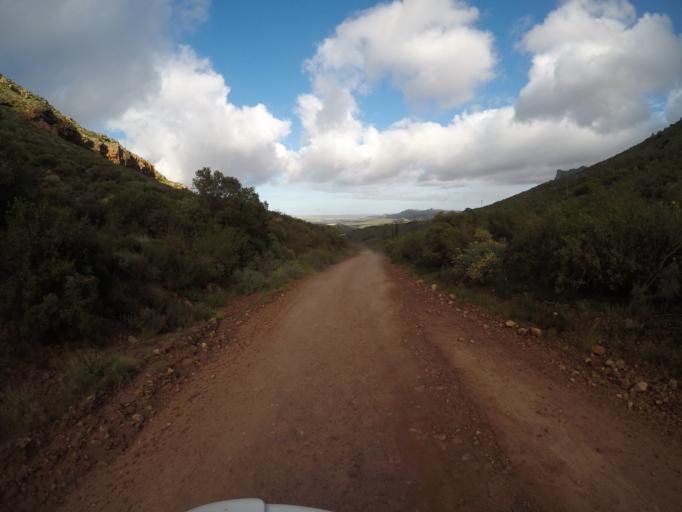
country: ZA
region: Western Cape
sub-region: West Coast District Municipality
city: Clanwilliam
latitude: -32.3402
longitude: 18.7833
